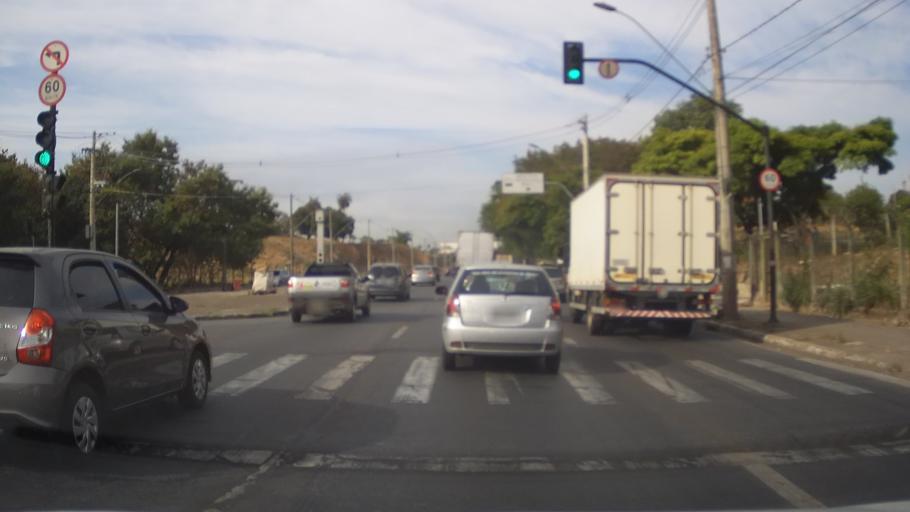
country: BR
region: Minas Gerais
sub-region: Contagem
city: Contagem
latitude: -19.8952
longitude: -44.0417
